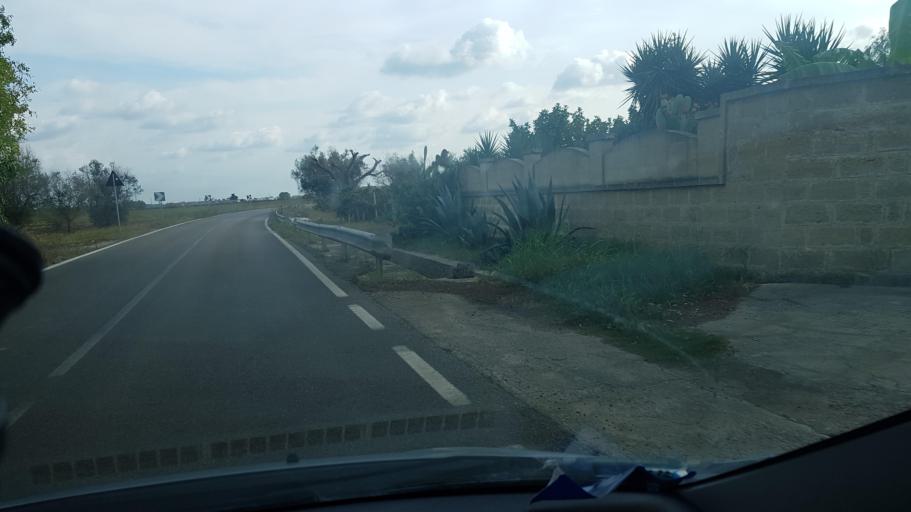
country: IT
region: Apulia
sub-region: Provincia di Brindisi
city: Cellino San Marco
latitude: 40.4438
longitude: 17.9545
